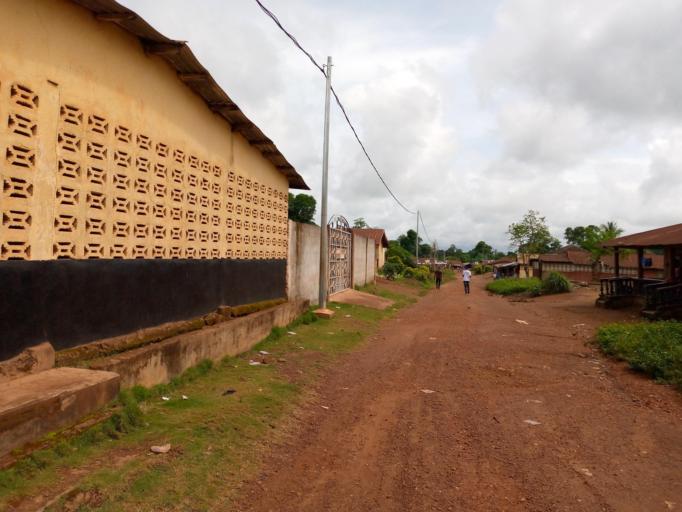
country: SL
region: Southern Province
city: Mogbwemo
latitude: 7.7616
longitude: -12.3078
